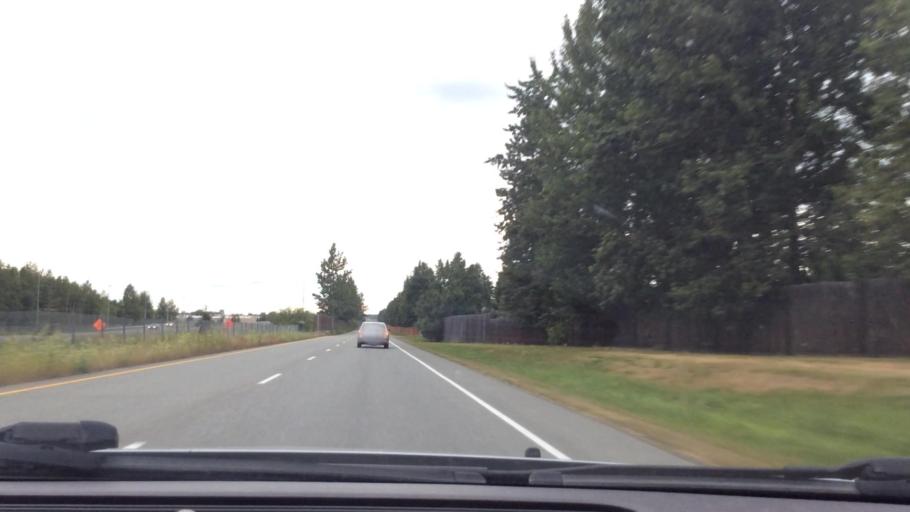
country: US
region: Alaska
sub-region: Anchorage Municipality
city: Anchorage
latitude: 61.1321
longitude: -149.8558
